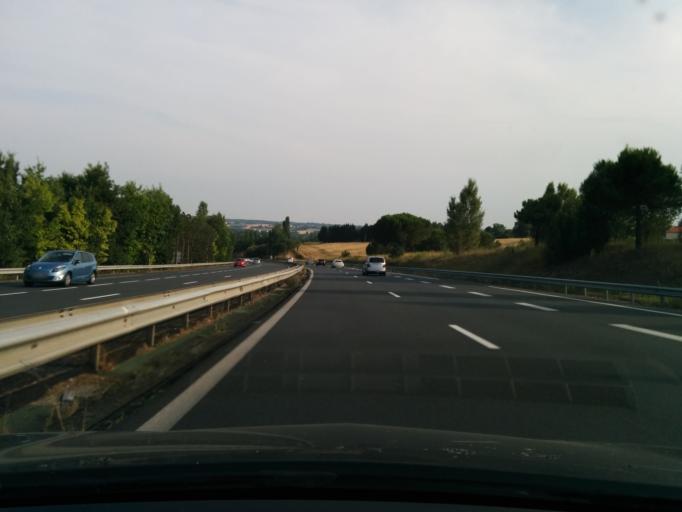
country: FR
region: Midi-Pyrenees
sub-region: Departement de la Haute-Garonne
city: Garidech
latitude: 43.7141
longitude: 1.5655
